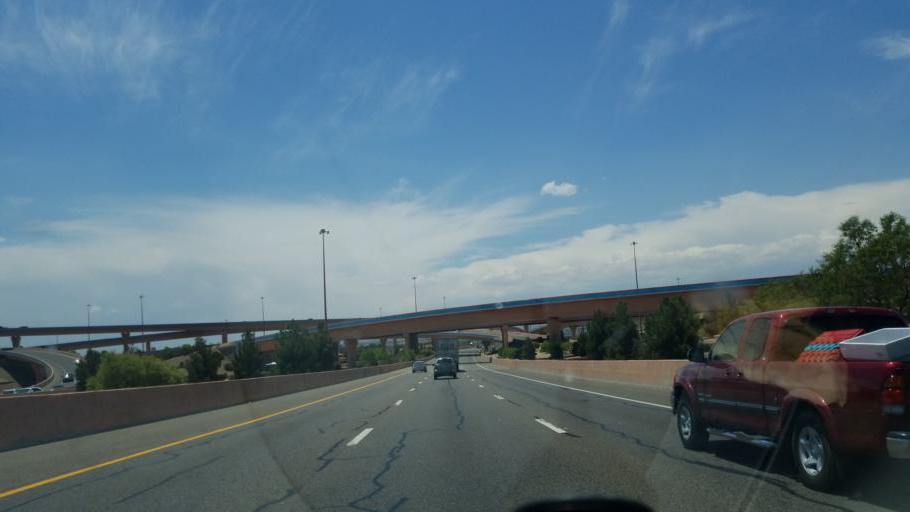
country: US
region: New Mexico
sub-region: Bernalillo County
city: Albuquerque
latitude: 35.1060
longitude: -106.6262
